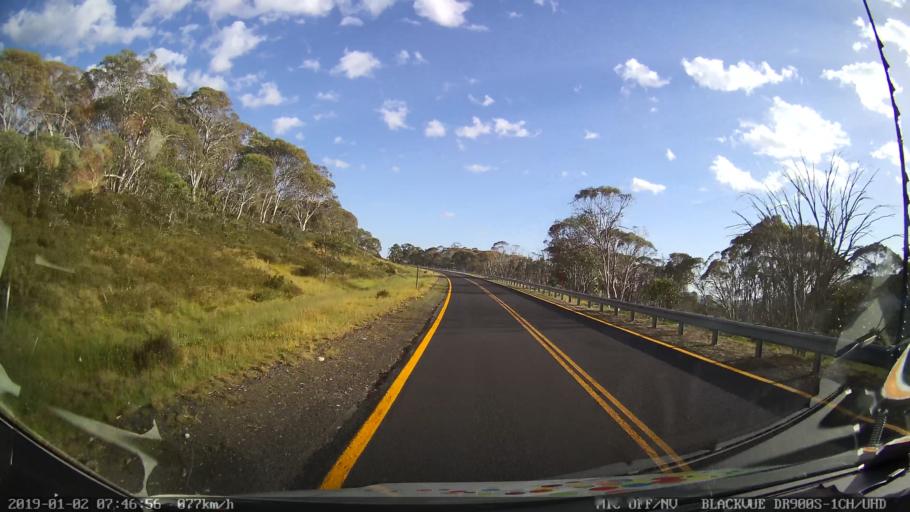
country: AU
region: New South Wales
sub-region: Tumut Shire
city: Tumut
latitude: -35.7704
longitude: 148.5211
